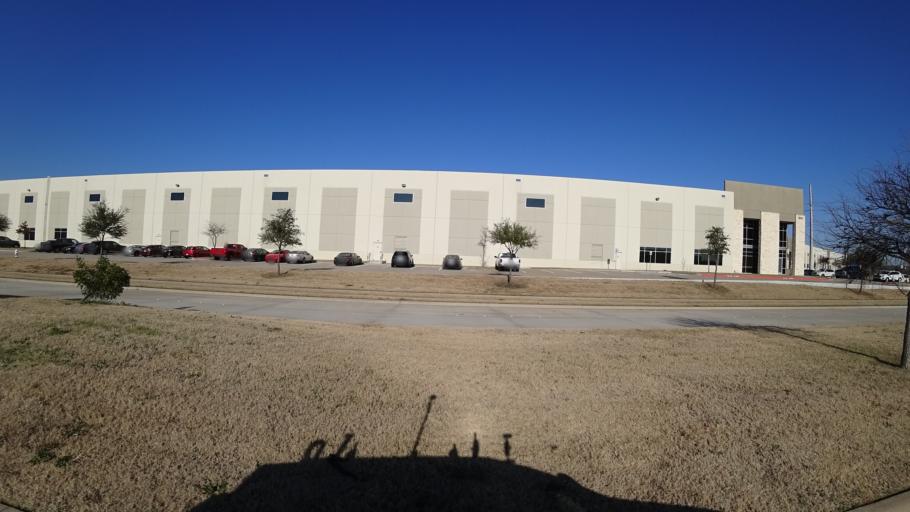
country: US
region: Texas
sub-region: Dallas County
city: Coppell
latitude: 32.9931
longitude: -97.0124
